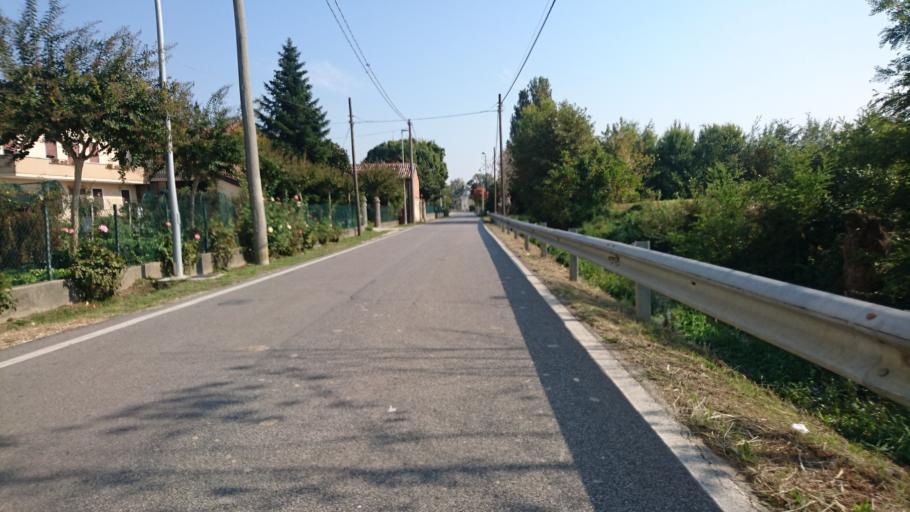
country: IT
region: Veneto
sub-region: Provincia di Vicenza
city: Grumolo delle Abbadesse
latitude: 45.5385
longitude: 11.6810
